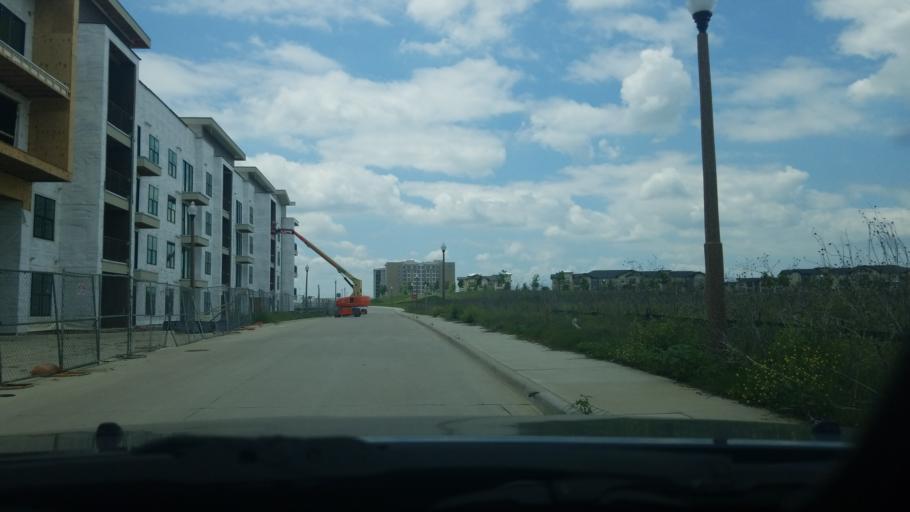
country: US
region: Texas
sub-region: Denton County
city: Denton
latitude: 33.2239
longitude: -97.1630
